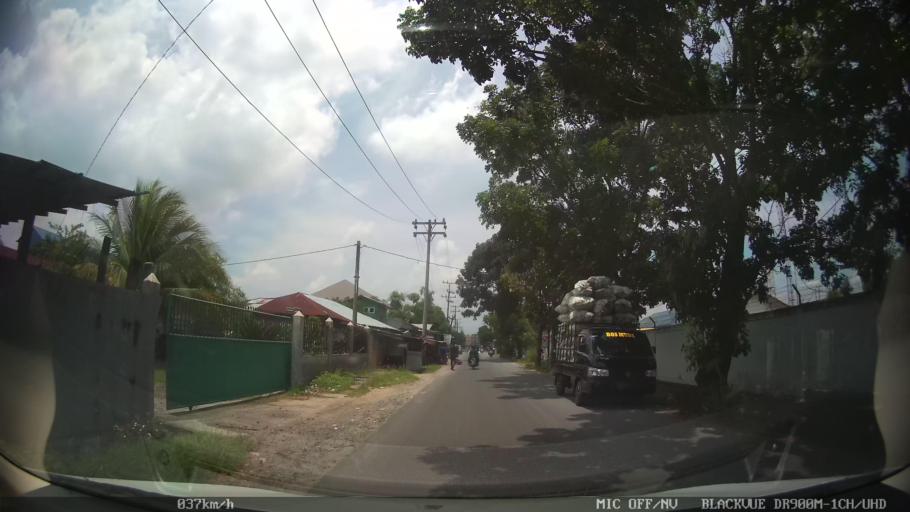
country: ID
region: North Sumatra
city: Labuhan Deli
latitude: 3.7100
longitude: 98.6652
